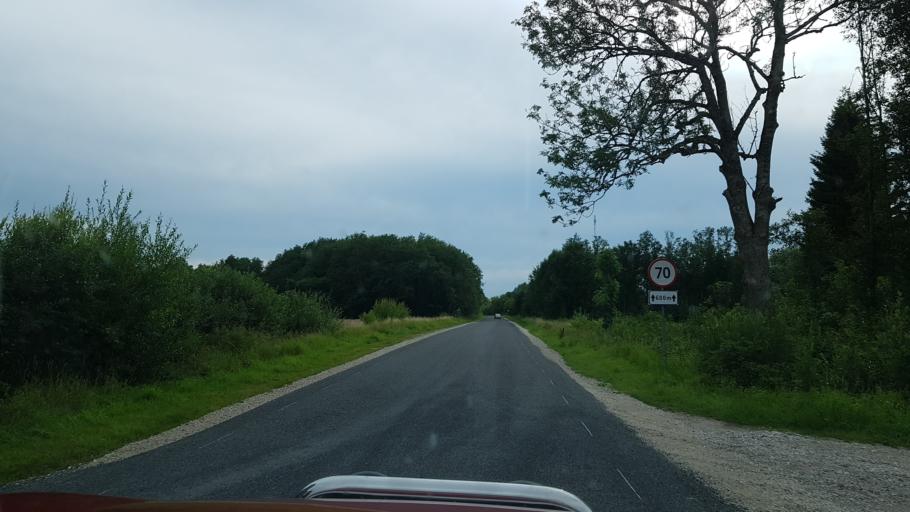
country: EE
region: Laeaene
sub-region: Lihula vald
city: Lihula
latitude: 58.8893
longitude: 23.8758
